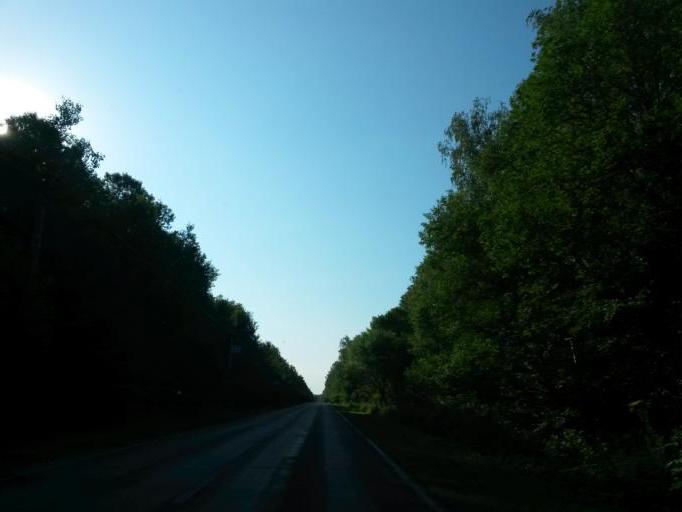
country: RU
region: Moskovskaya
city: Melikhovo
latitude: 55.2237
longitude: 37.6616
